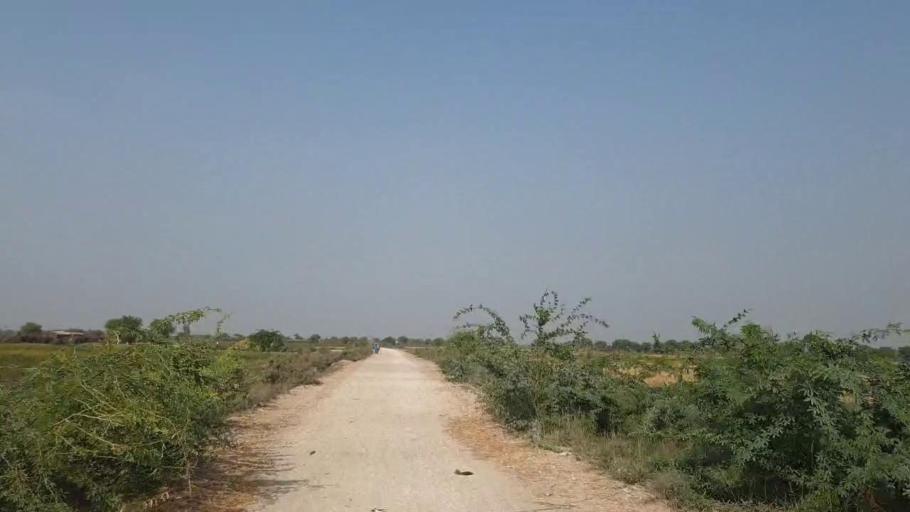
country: PK
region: Sindh
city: Kario
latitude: 24.9413
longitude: 68.5571
